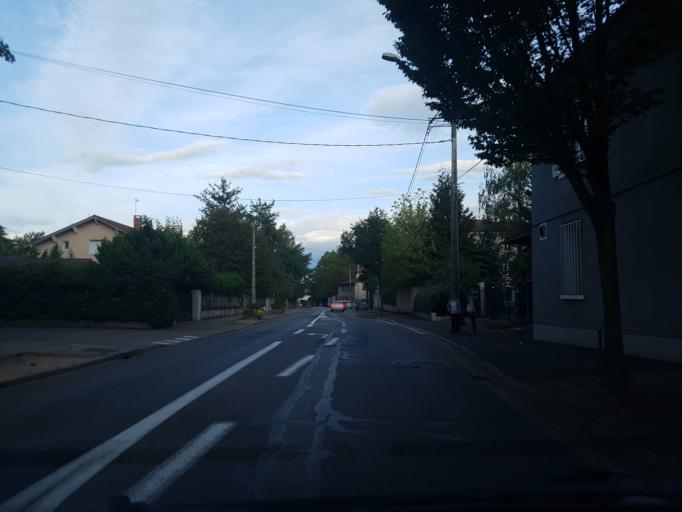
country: FR
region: Rhone-Alpes
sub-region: Departement du Rhone
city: Ecully
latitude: 45.7636
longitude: 4.7645
